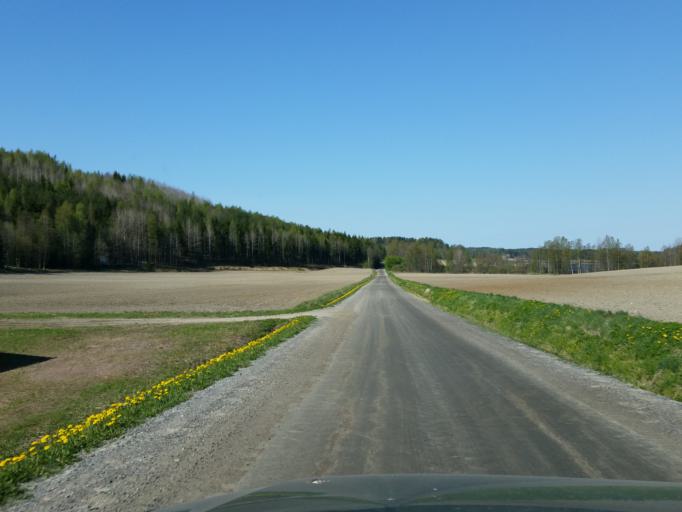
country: FI
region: Uusimaa
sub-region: Helsinki
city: Karjalohja
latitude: 60.1461
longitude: 23.7916
